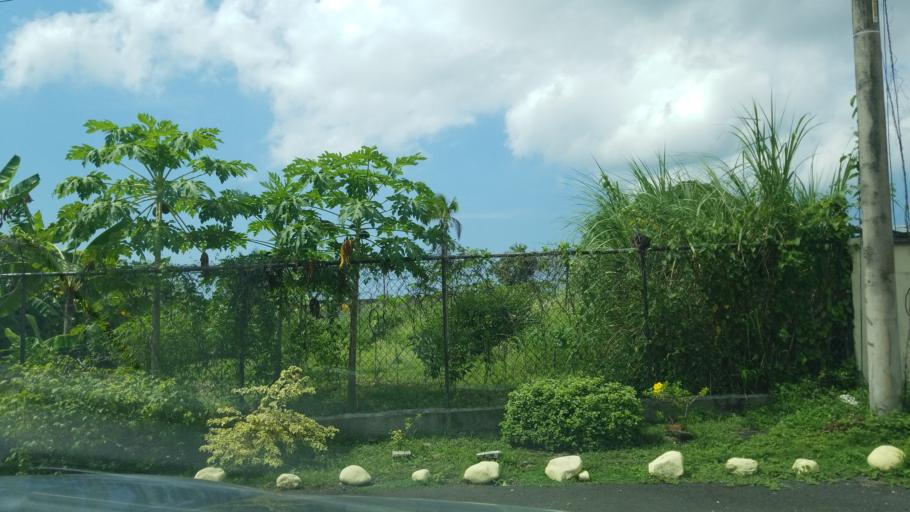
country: PA
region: Panama
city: San Miguelito
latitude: 9.0397
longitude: -79.4318
